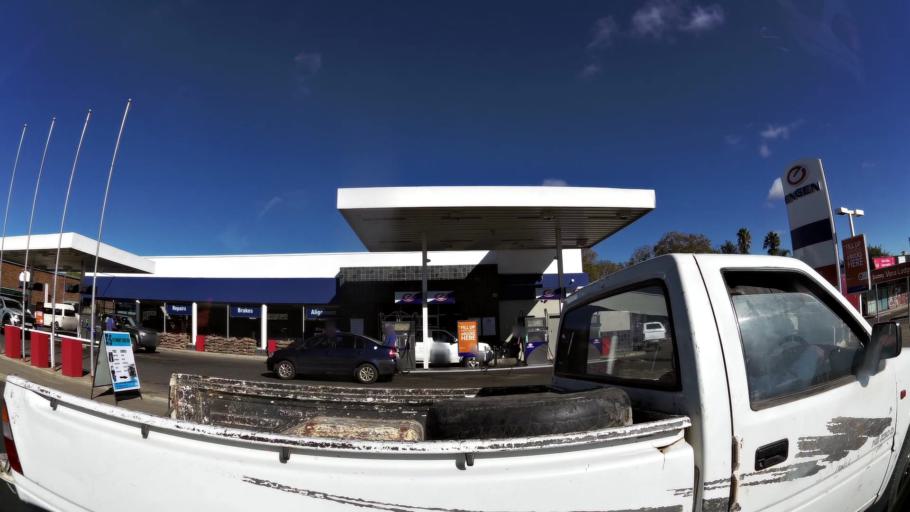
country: ZA
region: Limpopo
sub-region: Capricorn District Municipality
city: Polokwane
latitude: -23.8795
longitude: 29.4419
